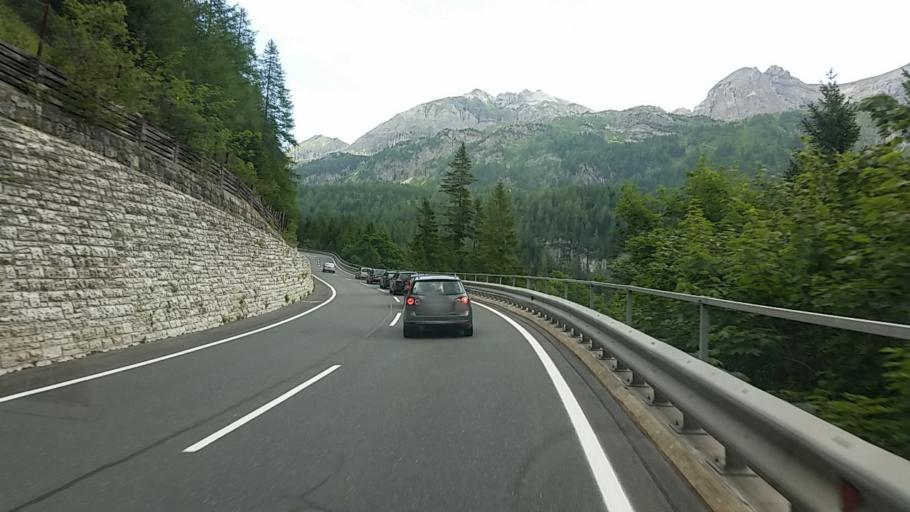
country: AT
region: Salzburg
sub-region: Politischer Bezirk Sankt Johann im Pongau
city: Untertauern
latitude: 47.2553
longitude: 13.5020
